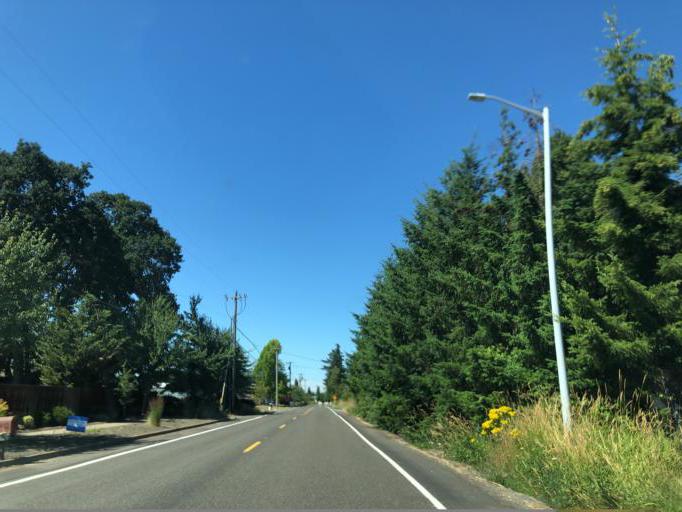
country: US
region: Oregon
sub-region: Marion County
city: Silverton
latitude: 45.0180
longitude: -122.7688
